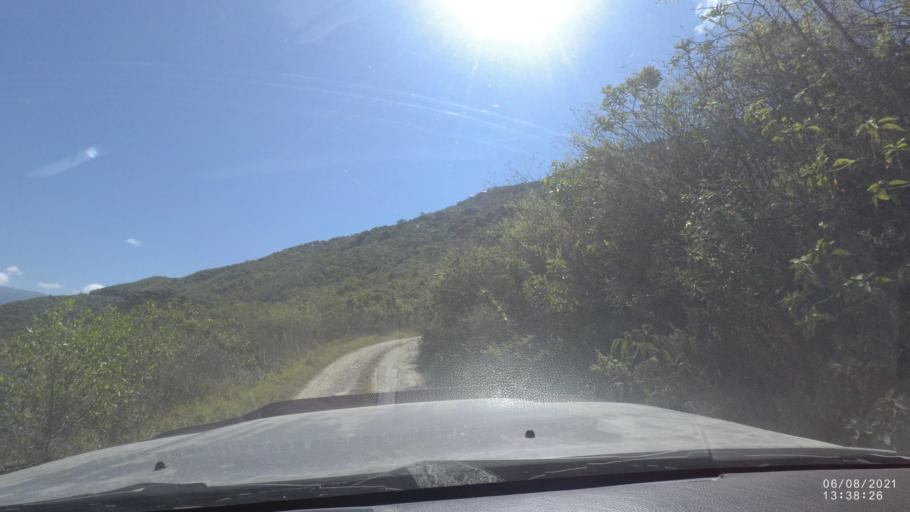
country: BO
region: La Paz
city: Quime
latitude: -16.6871
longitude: -66.7253
